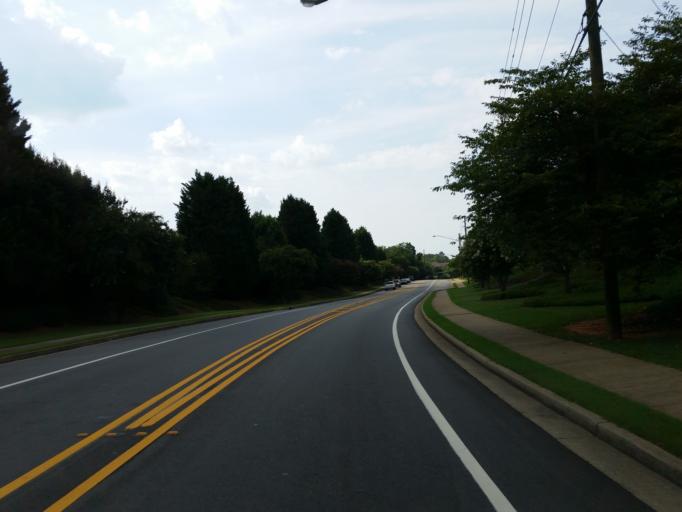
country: US
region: Georgia
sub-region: Fulton County
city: Roswell
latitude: 34.0518
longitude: -84.3819
